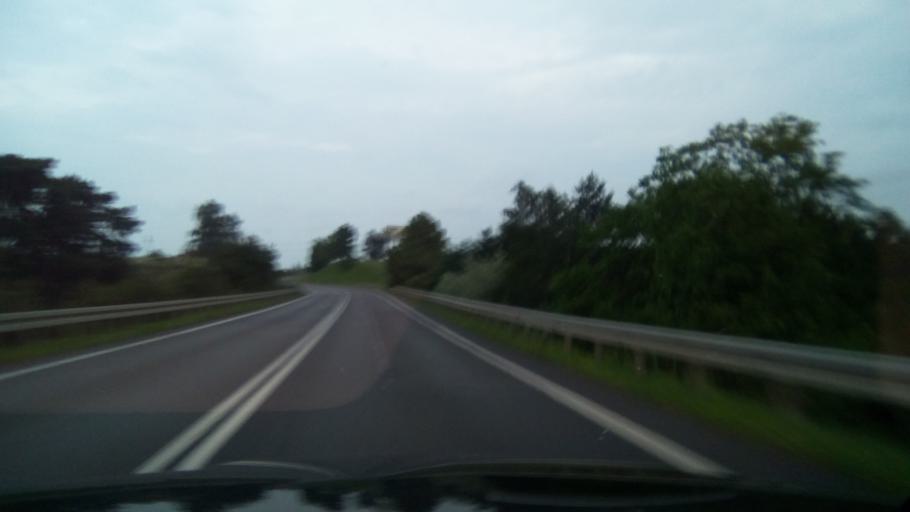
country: PL
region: Greater Poland Voivodeship
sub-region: Powiat gnieznienski
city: Lubowo
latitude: 52.5122
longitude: 17.4355
